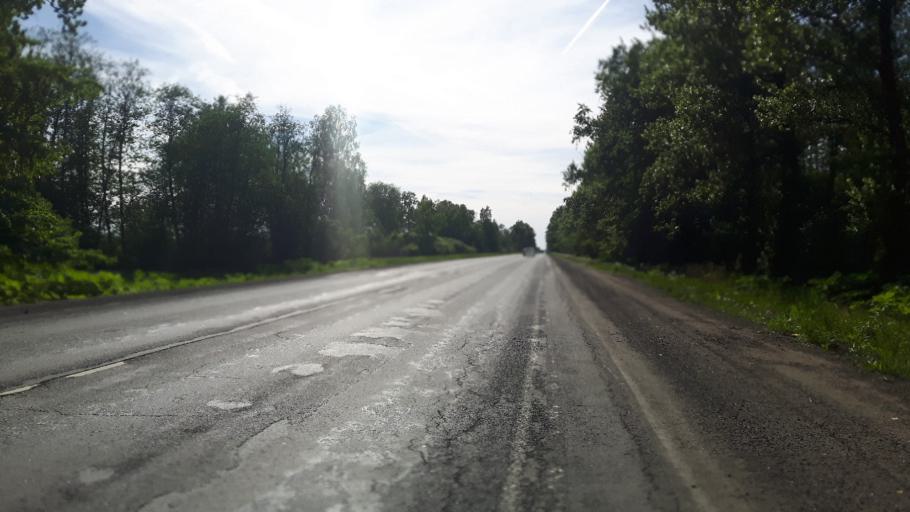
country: RU
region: Leningrad
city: Ivangorod
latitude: 59.3817
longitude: 28.3505
